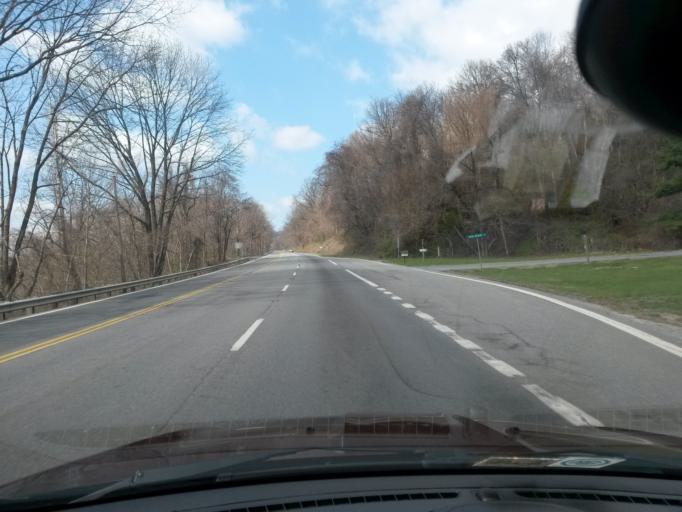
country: US
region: Virginia
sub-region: City of Waynesboro
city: Waynesboro
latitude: 38.0365
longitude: -78.8406
